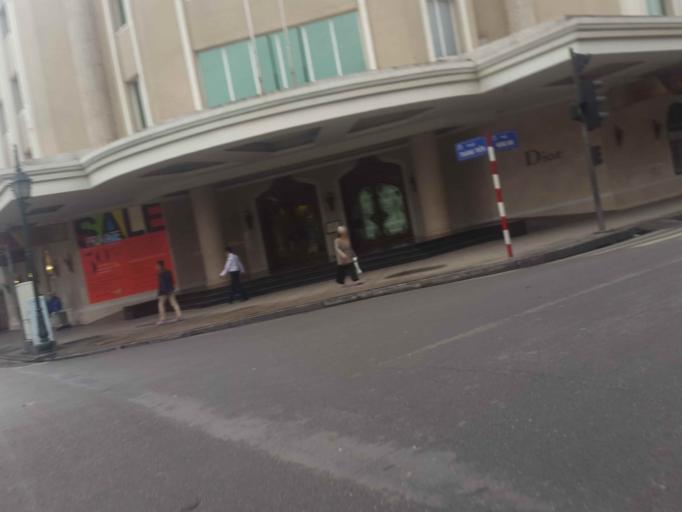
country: VN
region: Ha Noi
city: Hoan Kiem
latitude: 21.0255
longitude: 105.8531
